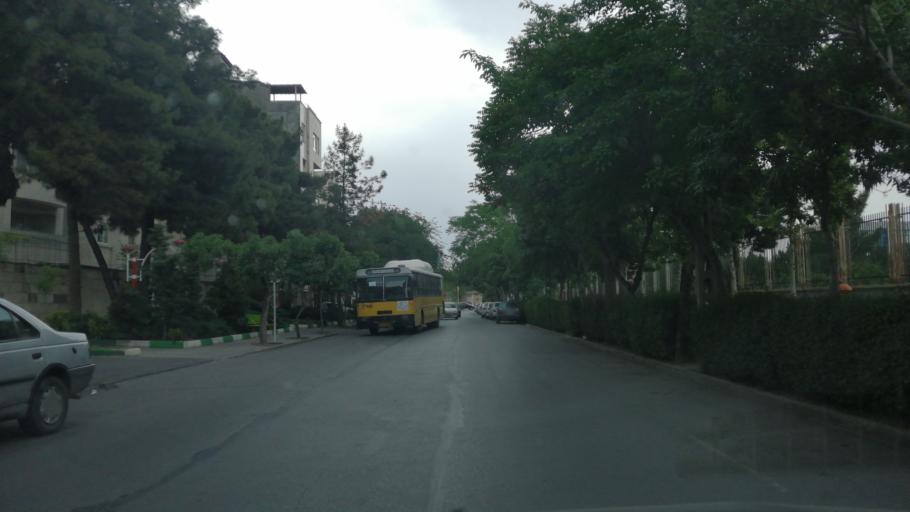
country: IR
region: Razavi Khorasan
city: Mashhad
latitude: 36.2874
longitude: 59.5818
